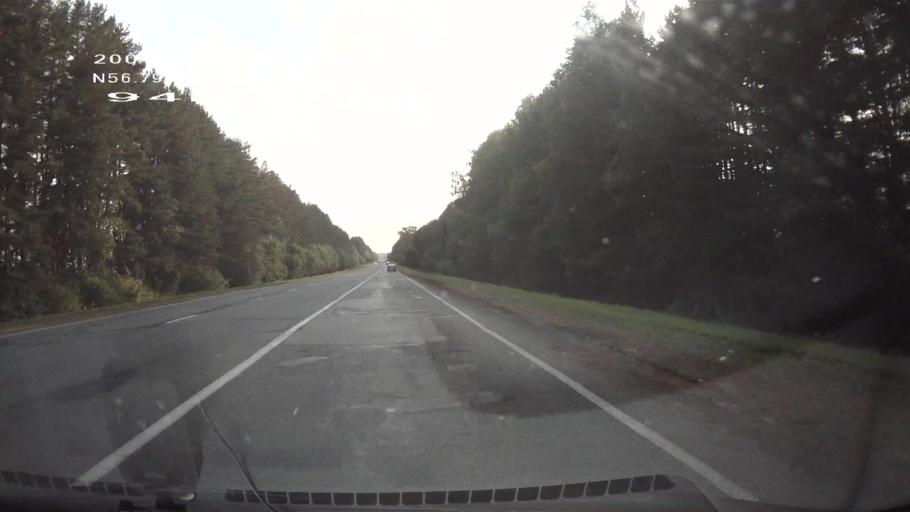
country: RU
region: Mariy-El
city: Sovetskiy
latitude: 56.7899
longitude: 48.6746
